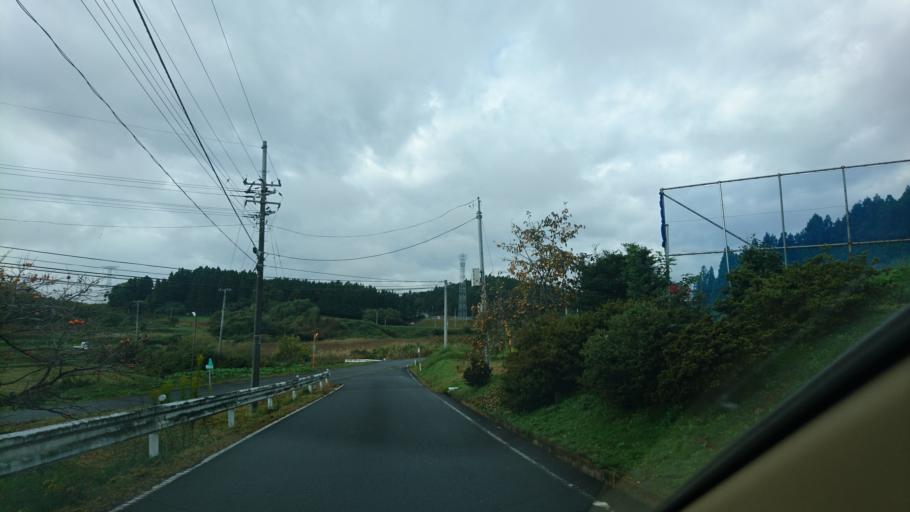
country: JP
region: Iwate
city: Ichinoseki
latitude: 38.7924
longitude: 140.9842
